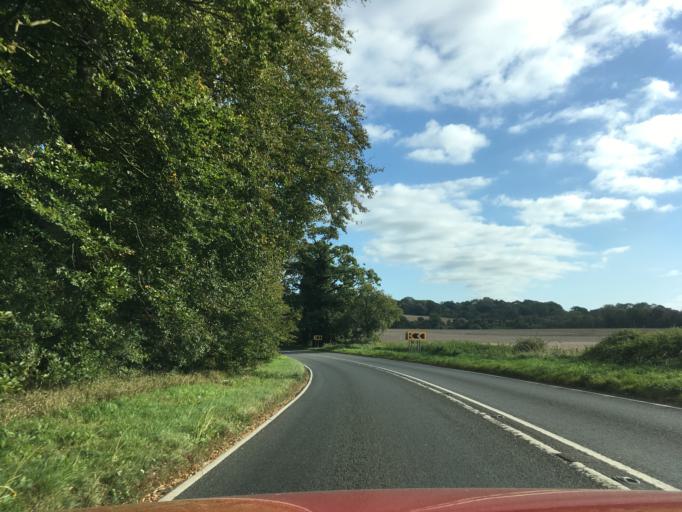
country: GB
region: England
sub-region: Hampshire
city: Basingstoke
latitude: 51.2340
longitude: -1.0766
